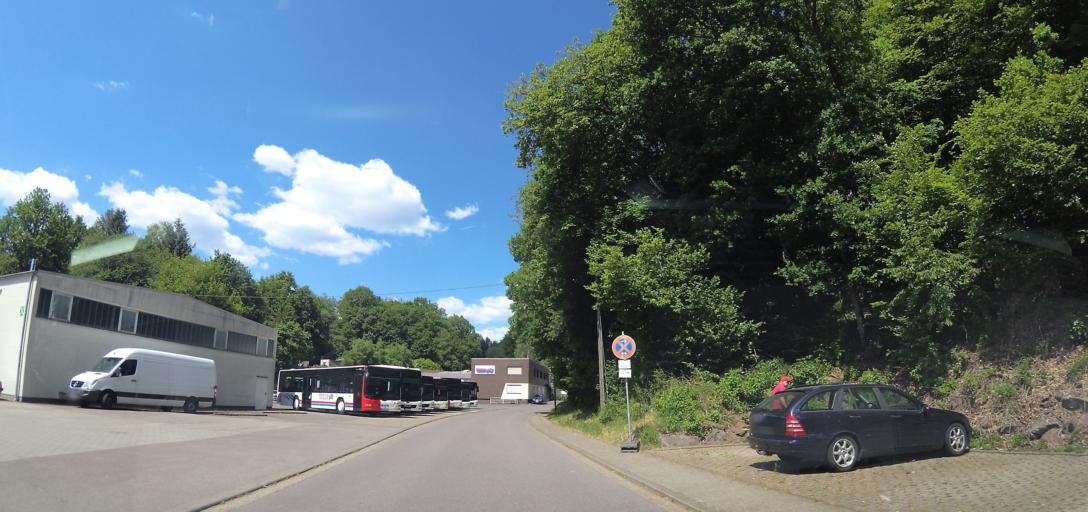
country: DE
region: Saarland
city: Wadern
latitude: 49.5283
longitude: 6.9324
